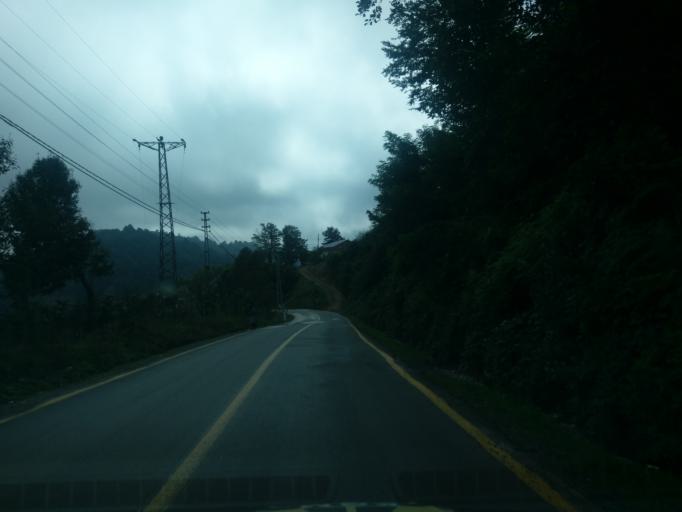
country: TR
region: Ordu
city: Gurgentepe
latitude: 40.8496
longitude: 37.6564
